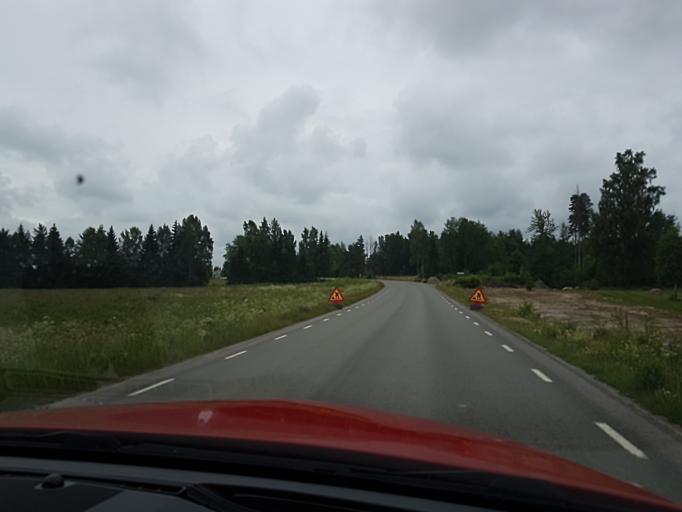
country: SE
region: Vaestra Goetaland
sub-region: Tidaholms Kommun
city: Olofstorp
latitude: 58.3483
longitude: 13.9624
